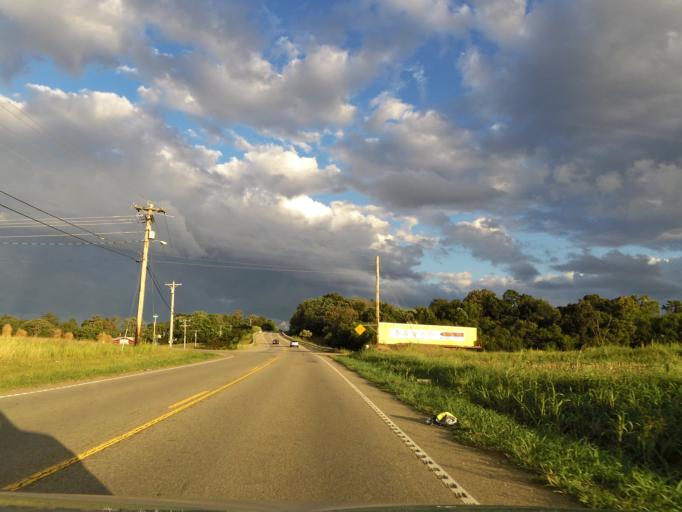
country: US
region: Tennessee
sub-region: Jefferson County
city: Jefferson City
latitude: 36.1227
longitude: -83.5117
